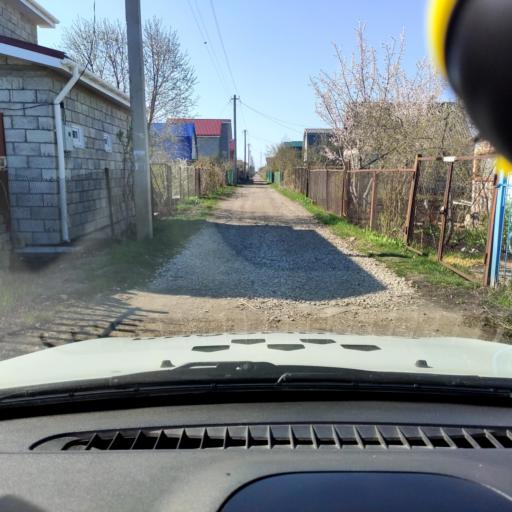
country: RU
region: Samara
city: Tol'yatti
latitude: 53.5981
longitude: 49.2949
